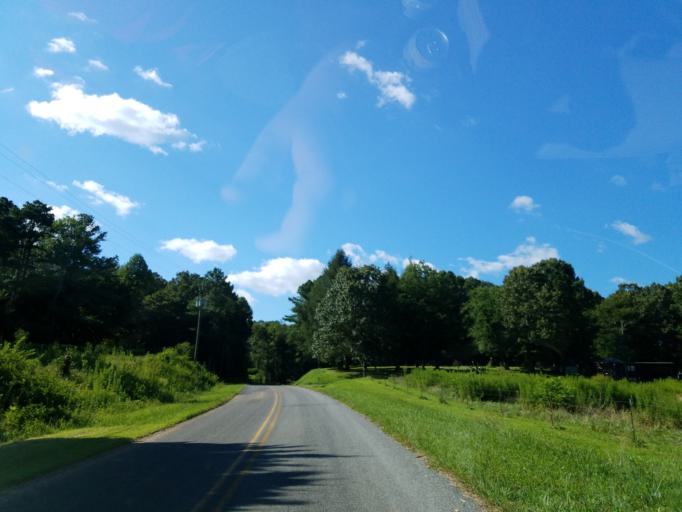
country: US
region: Georgia
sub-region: Gilmer County
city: Ellijay
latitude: 34.6478
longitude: -84.3399
